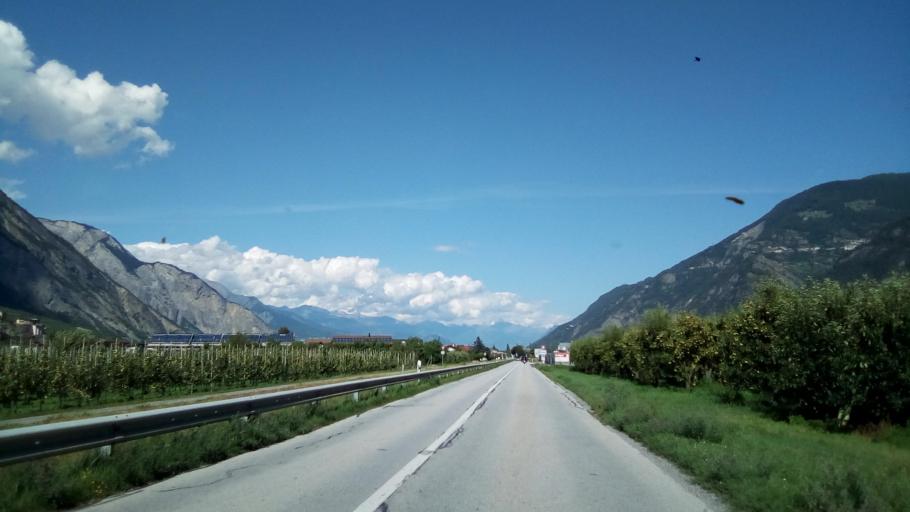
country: CH
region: Valais
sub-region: Martigny District
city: Saillon
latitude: 46.1639
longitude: 7.1794
